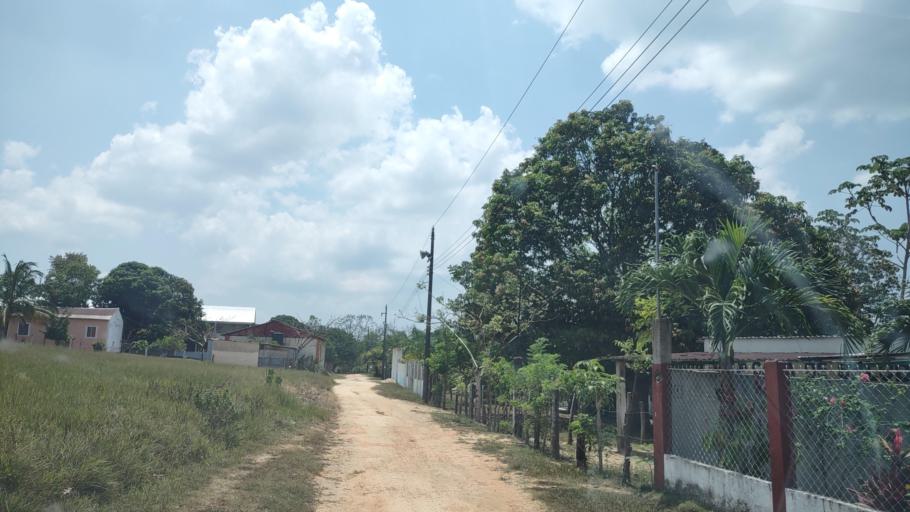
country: MX
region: Veracruz
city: Las Choapas
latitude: 17.9296
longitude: -94.1506
